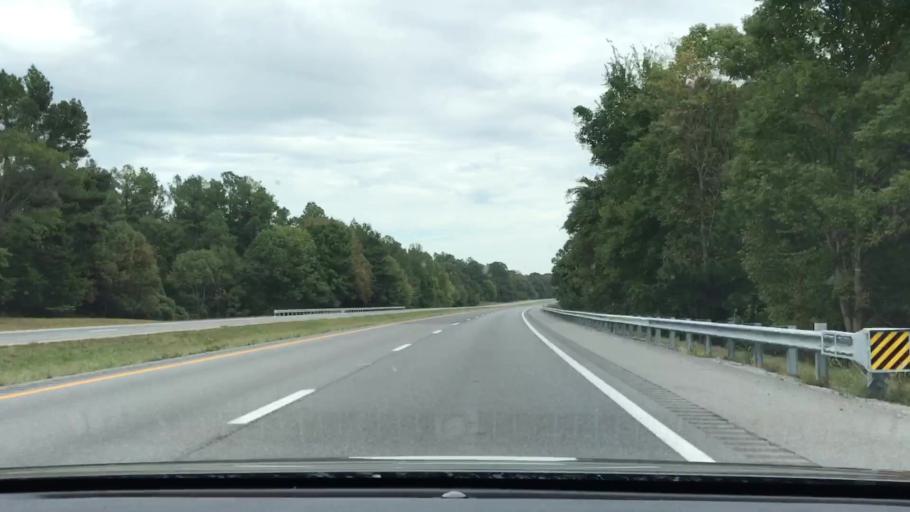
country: US
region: Kentucky
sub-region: Graves County
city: Mayfield
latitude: 36.7855
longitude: -88.5462
